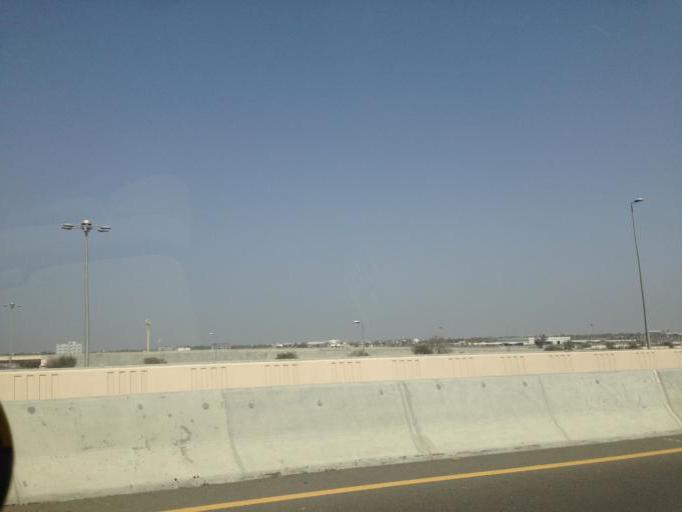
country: OM
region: Al Batinah
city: Barka'
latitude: 23.6858
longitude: 58.0243
